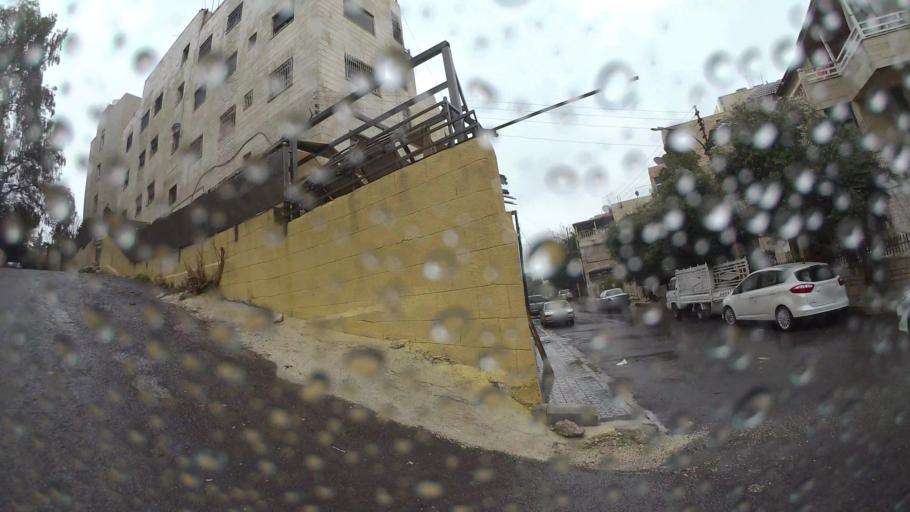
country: JO
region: Amman
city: Amman
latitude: 31.9580
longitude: 35.9109
